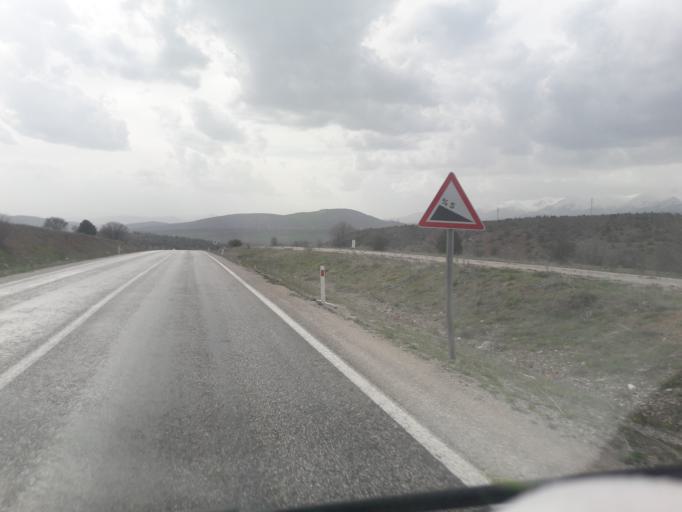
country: TR
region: Gumushane
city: Evren
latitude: 40.1713
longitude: 39.2435
